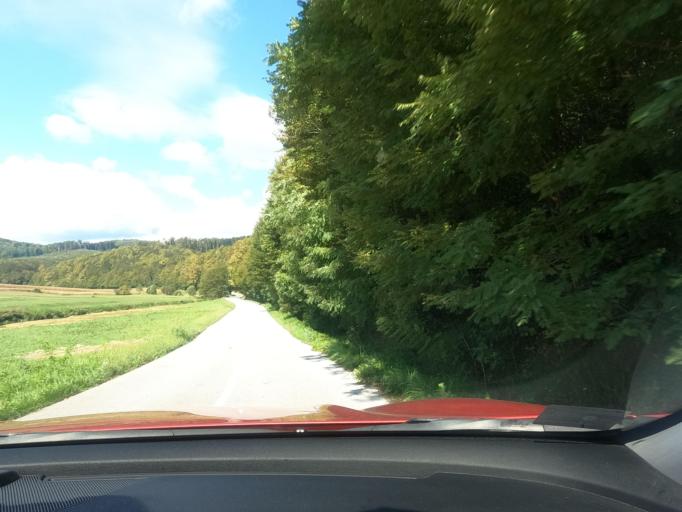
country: BA
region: Federation of Bosnia and Herzegovina
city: Podzvizd
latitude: 45.2229
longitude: 15.8507
